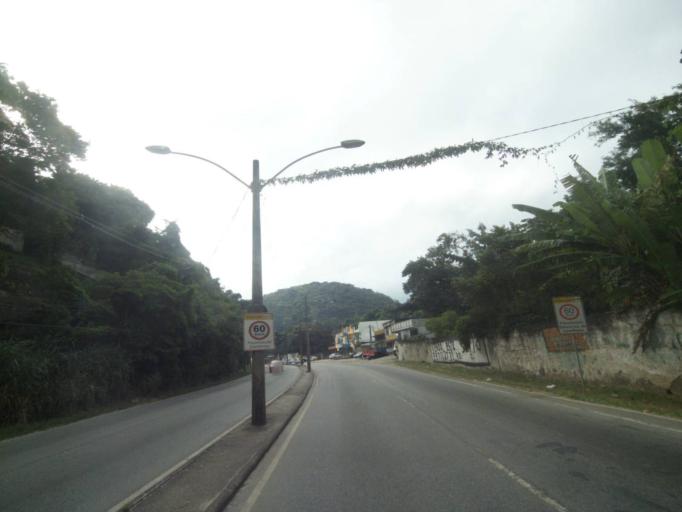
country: BR
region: Rio de Janeiro
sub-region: Sao Joao De Meriti
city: Sao Joao de Meriti
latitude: -22.9025
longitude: -43.3811
